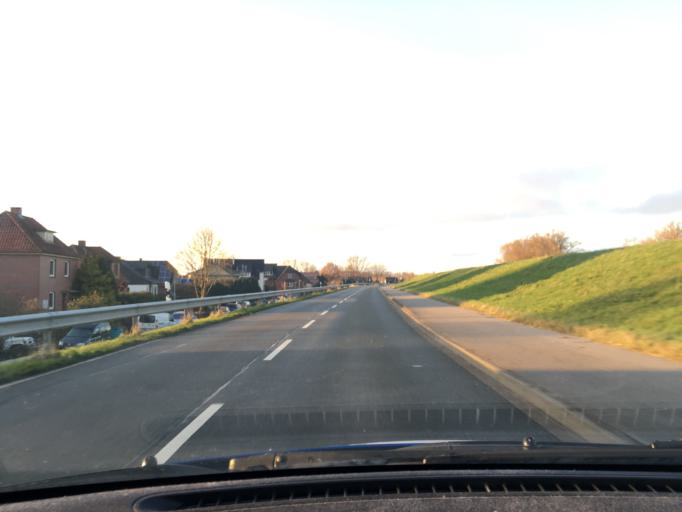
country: DE
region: Hamburg
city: Harburg
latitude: 53.4603
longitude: 10.0537
